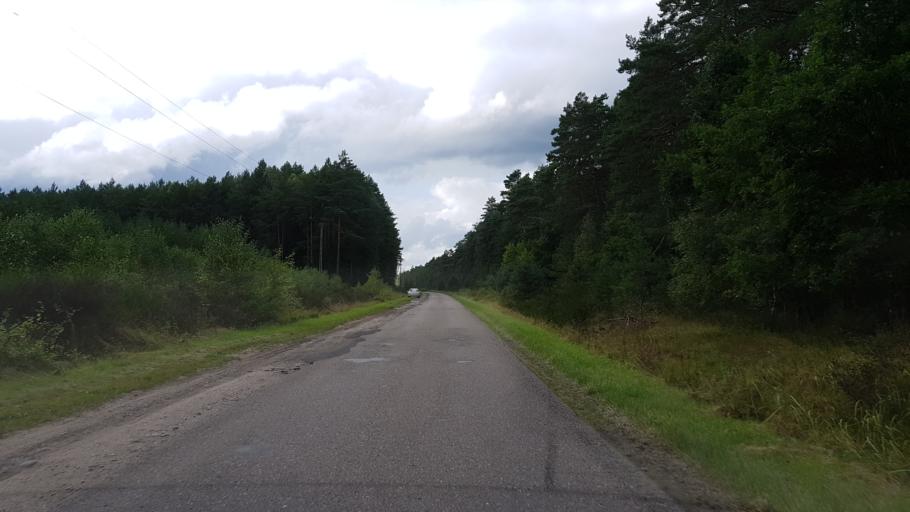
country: PL
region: West Pomeranian Voivodeship
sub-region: Powiat bialogardzki
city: Tychowo
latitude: 54.0334
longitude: 16.3436
